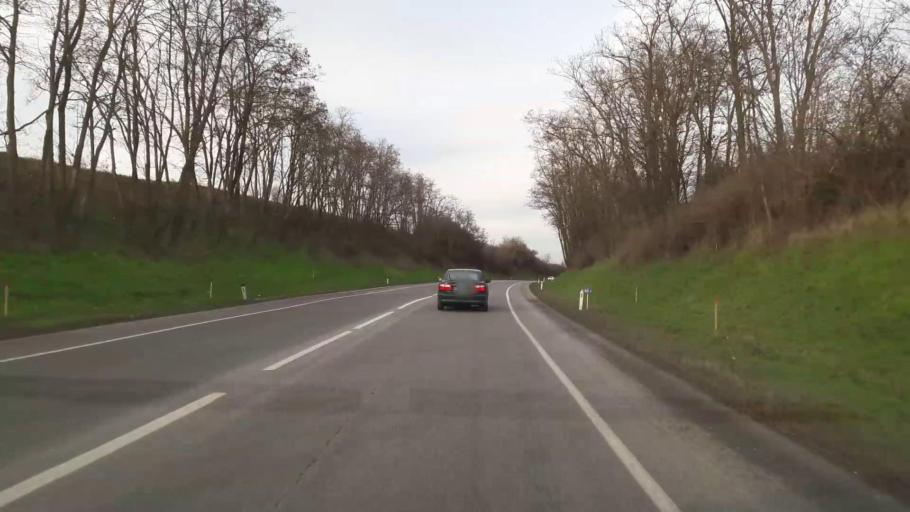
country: AT
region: Lower Austria
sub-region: Politischer Bezirk Mistelbach
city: Drasenhofen
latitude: 48.7341
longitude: 16.6562
